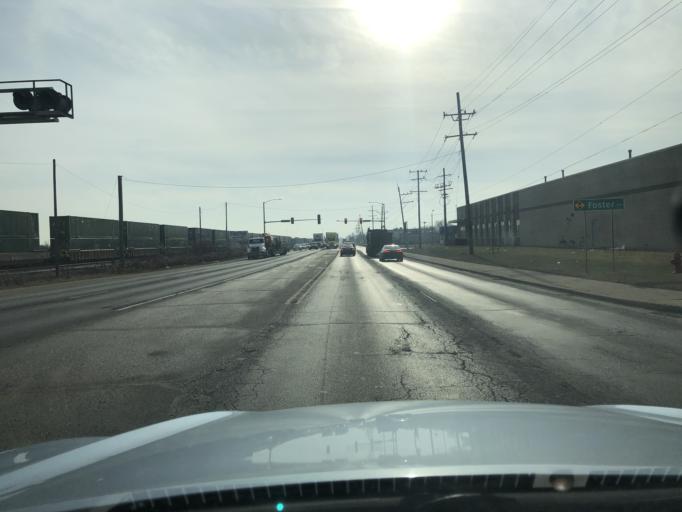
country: US
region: Illinois
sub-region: DuPage County
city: Bensenville
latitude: 41.9732
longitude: -87.9398
